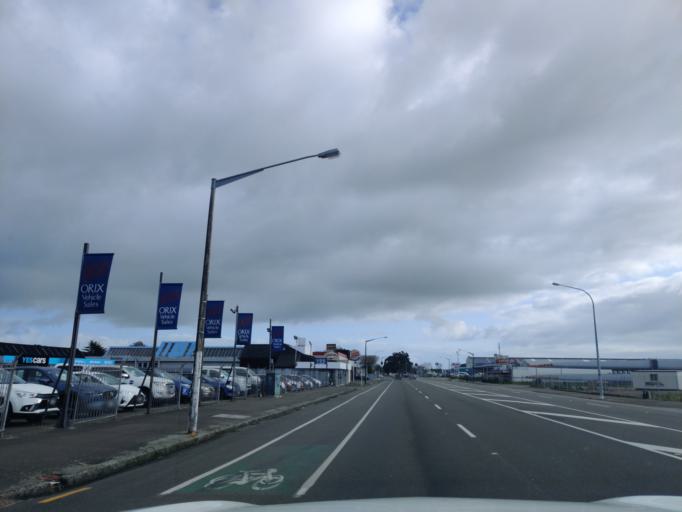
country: NZ
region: Manawatu-Wanganui
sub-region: Palmerston North City
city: Palmerston North
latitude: -40.3454
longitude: 175.6028
